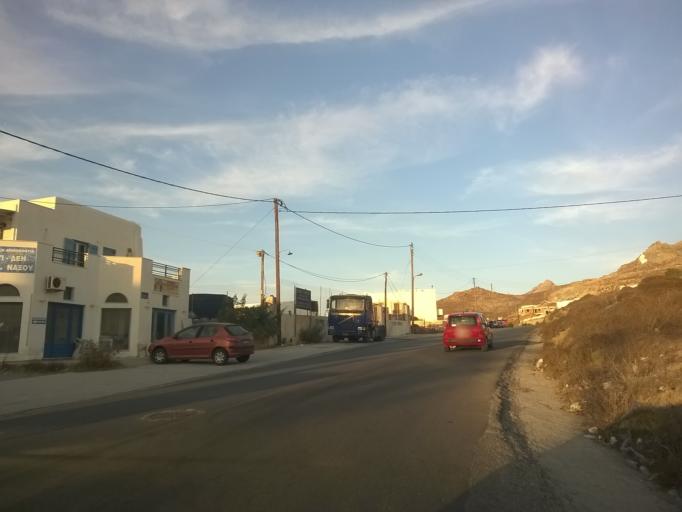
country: GR
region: South Aegean
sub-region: Nomos Kykladon
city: Naxos
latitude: 37.1097
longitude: 25.3841
